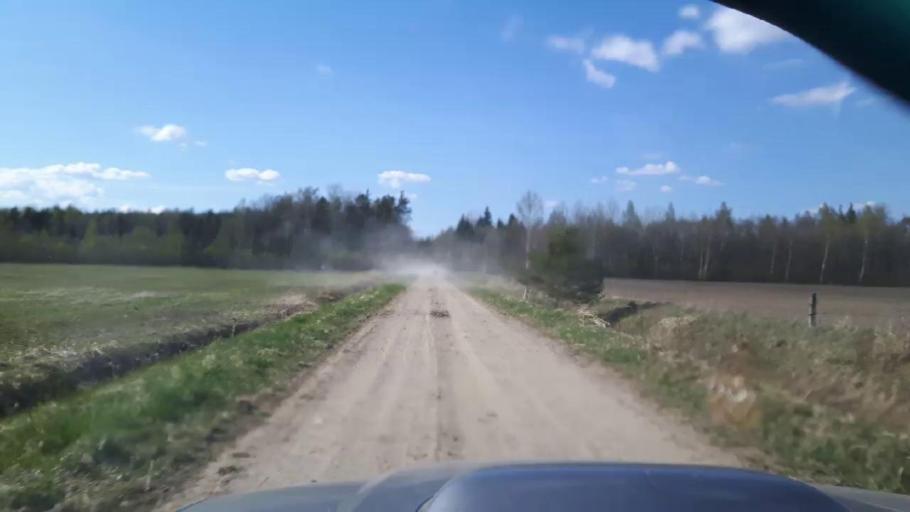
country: EE
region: Paernumaa
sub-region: Tootsi vald
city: Tootsi
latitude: 58.4431
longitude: 24.8765
